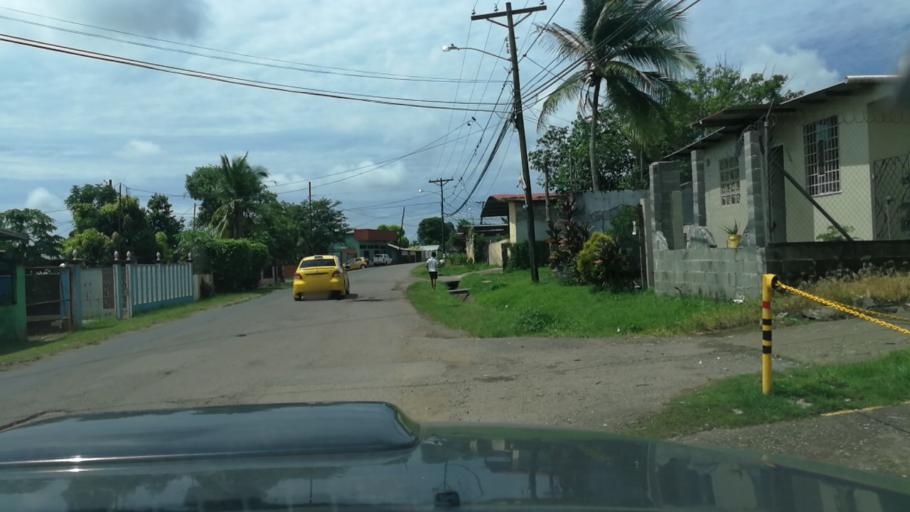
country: PA
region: Panama
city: Tocumen
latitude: 9.1024
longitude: -79.4117
